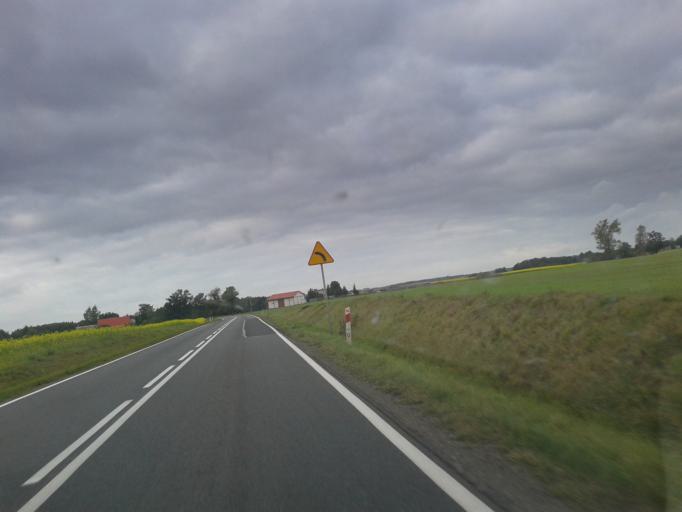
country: PL
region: Kujawsko-Pomorskie
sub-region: Powiat sepolenski
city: Sepolno Krajenskie
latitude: 53.4824
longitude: 17.5203
